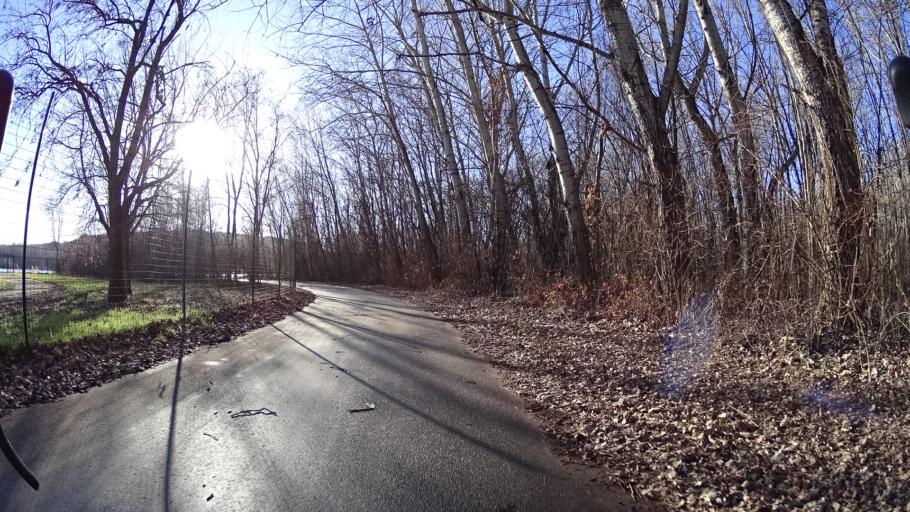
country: AT
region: Lower Austria
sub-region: Politischer Bezirk Krems
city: Gedersdorf
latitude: 48.3894
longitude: 15.6942
